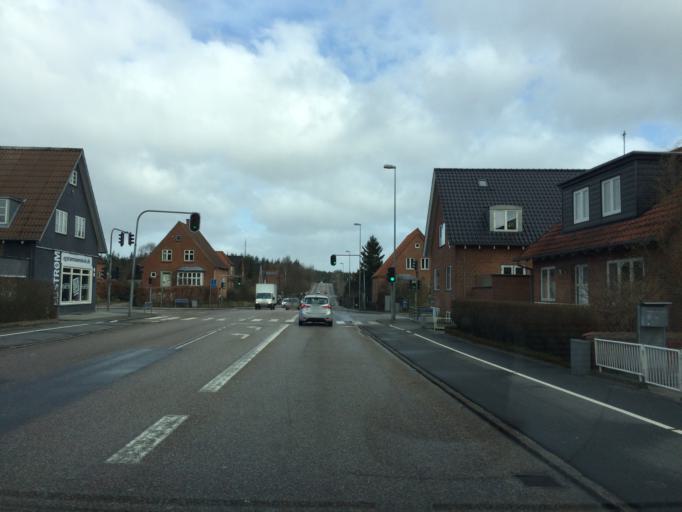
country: DK
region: Central Jutland
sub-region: Silkeborg Kommune
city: Silkeborg
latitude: 56.1586
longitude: 9.5313
